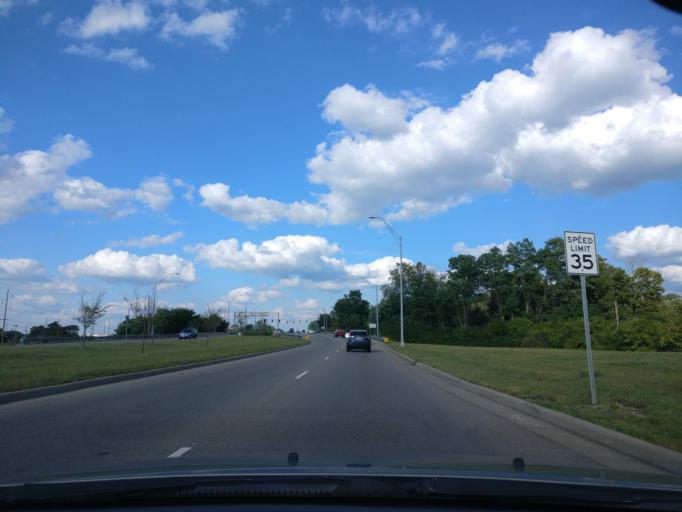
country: US
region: Ohio
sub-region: Montgomery County
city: Moraine
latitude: 39.6820
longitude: -84.2283
